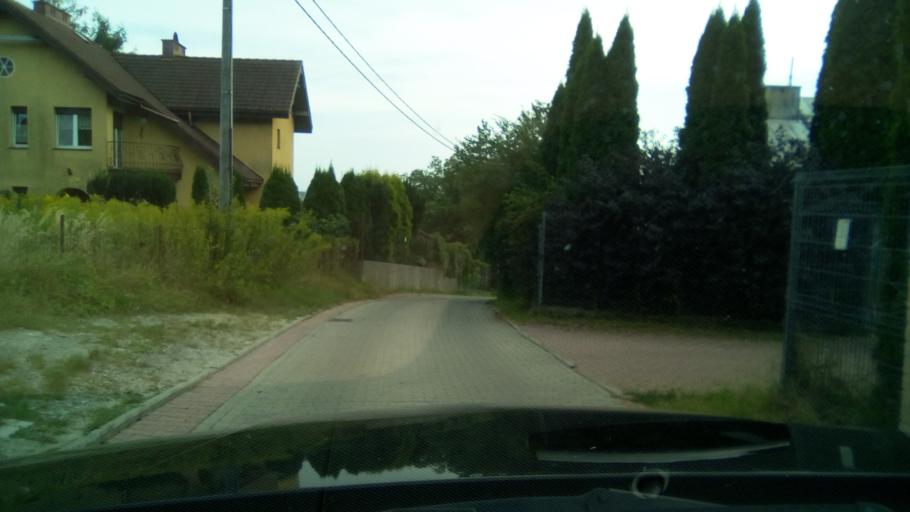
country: PL
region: Lesser Poland Voivodeship
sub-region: Krakow
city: Krakow
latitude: 50.0496
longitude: 19.8950
